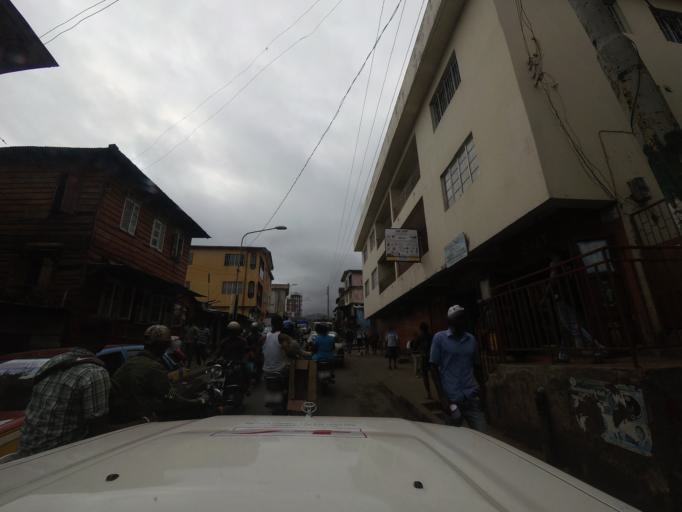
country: SL
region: Western Area
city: Freetown
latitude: 8.4838
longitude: -13.2438
